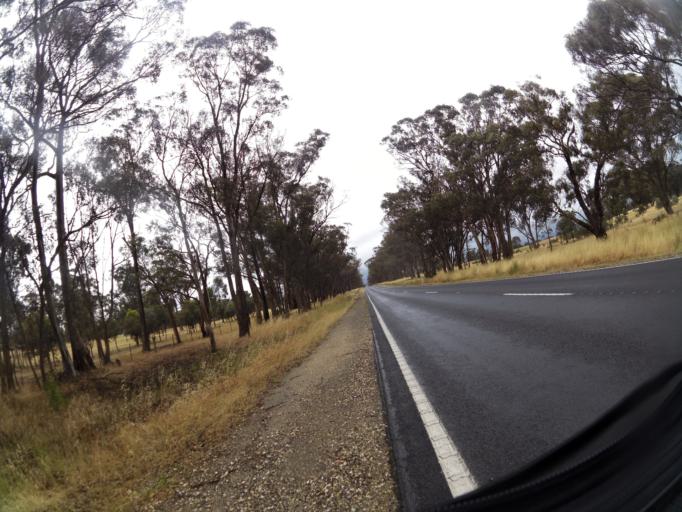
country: AU
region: Victoria
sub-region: Mount Alexander
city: Castlemaine
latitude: -37.0926
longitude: 144.1413
